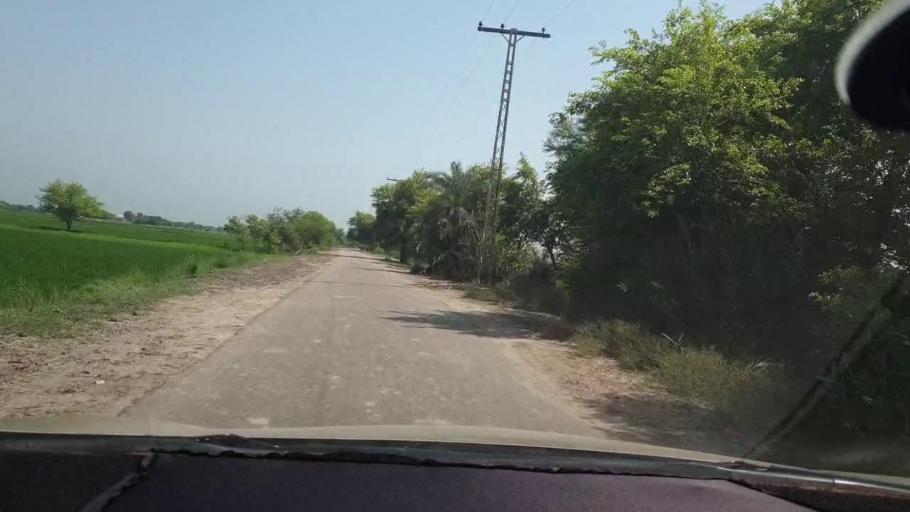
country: PK
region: Sindh
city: Kambar
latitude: 27.5035
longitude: 68.0153
